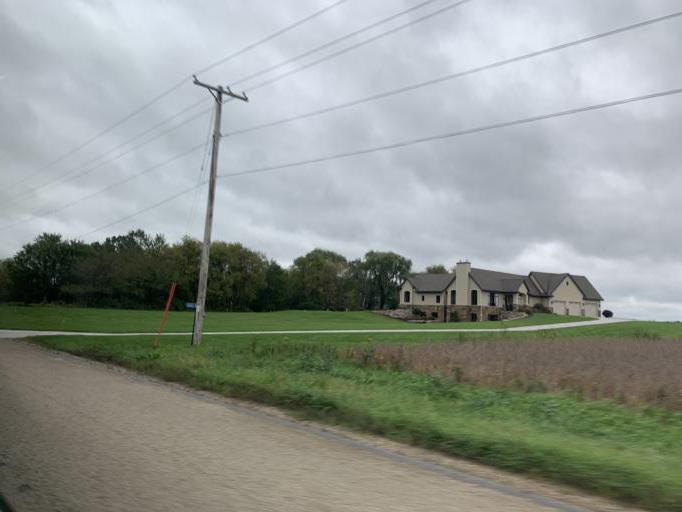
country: US
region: Wisconsin
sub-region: Sauk County
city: Prairie du Sac
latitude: 43.3417
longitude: -89.7661
